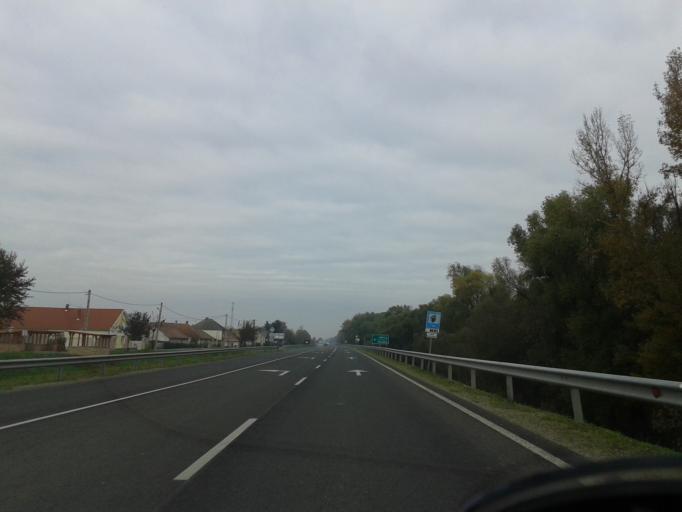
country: HU
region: Fejer
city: Adony
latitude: 47.1220
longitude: 18.8686
